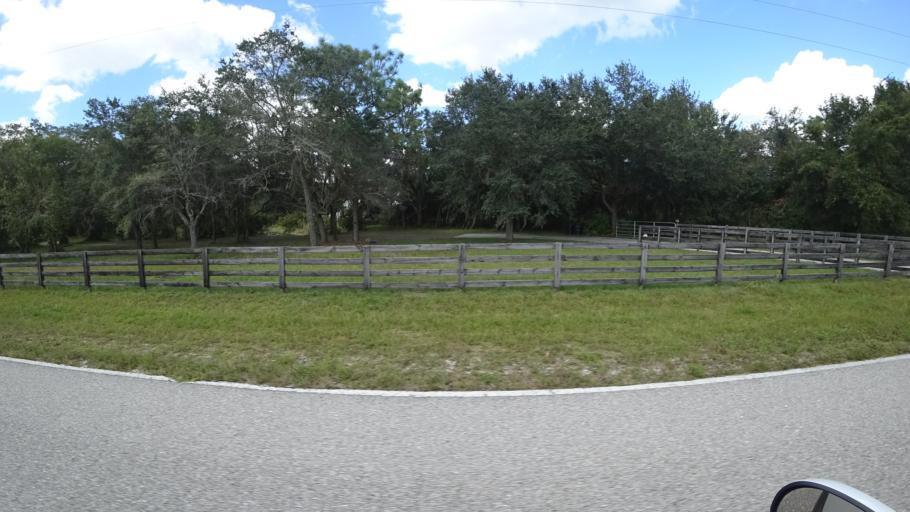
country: US
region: Florida
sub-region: Sarasota County
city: Lake Sarasota
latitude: 27.3330
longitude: -82.1652
